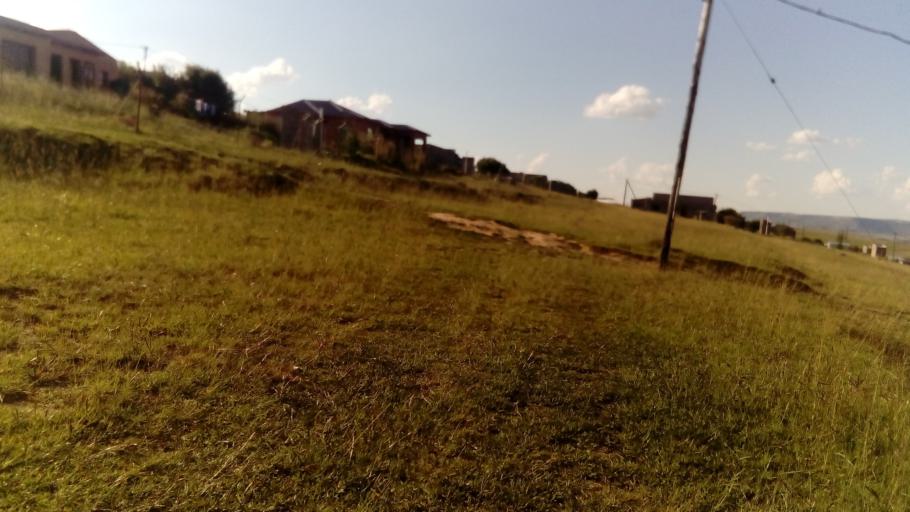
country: LS
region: Berea
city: Teyateyaneng
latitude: -29.1336
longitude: 27.7627
